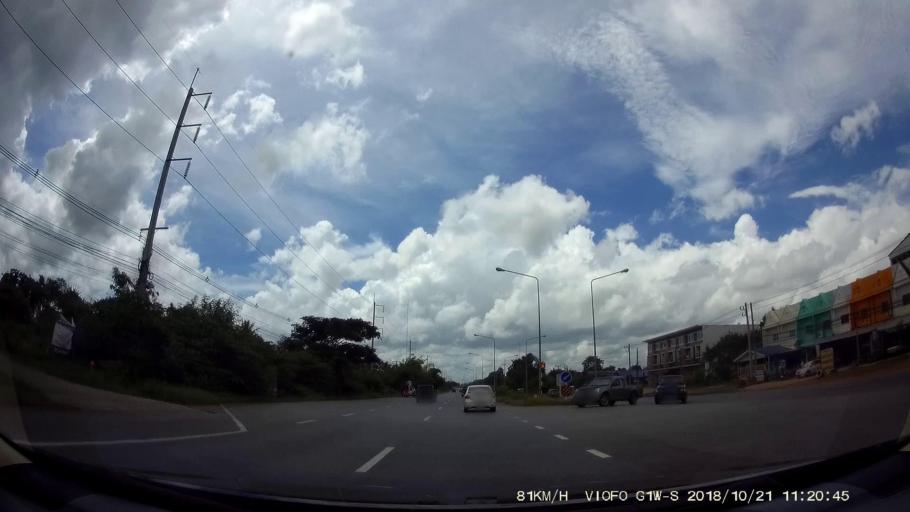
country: TH
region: Chaiyaphum
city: Chaiyaphum
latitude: 15.8537
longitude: 102.0719
